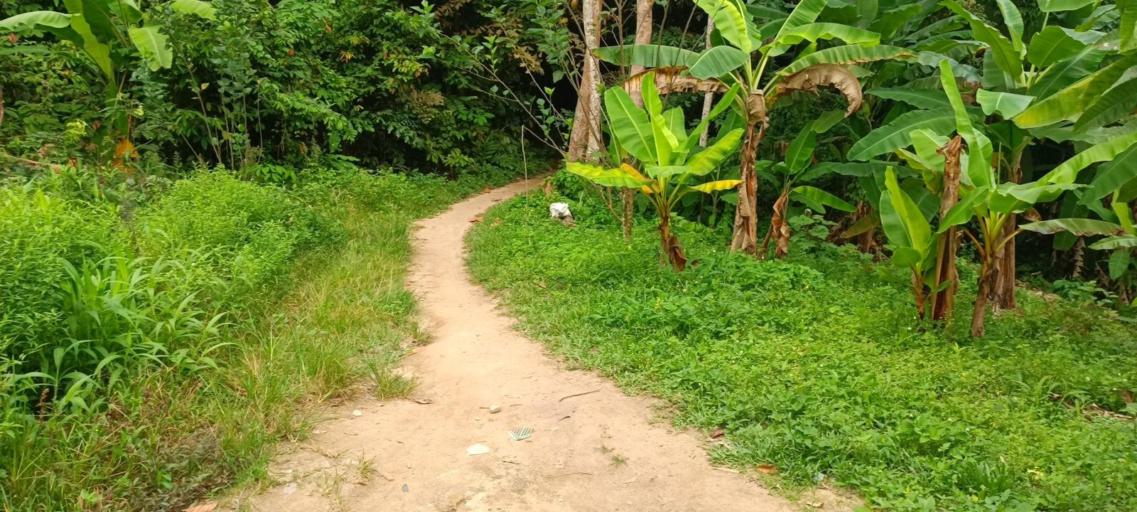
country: MY
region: Penang
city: Kampung Sungai Ara
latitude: 5.3471
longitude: 100.2849
